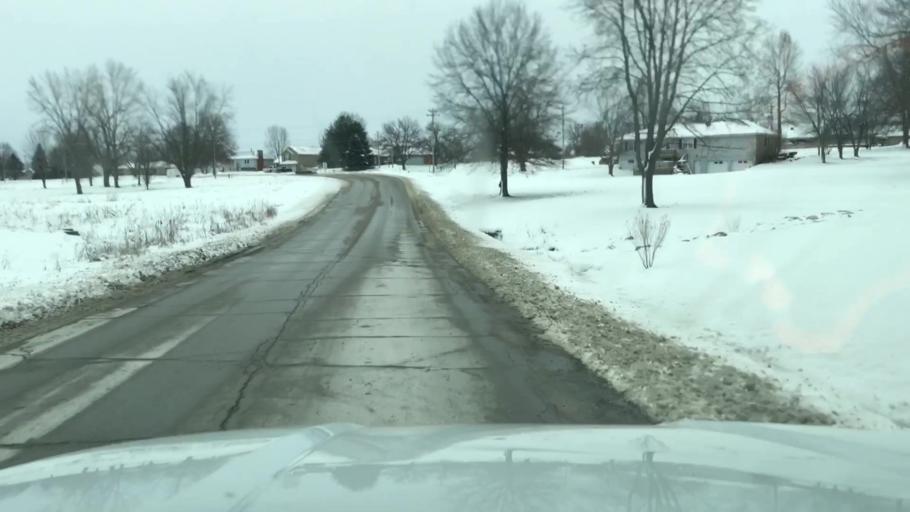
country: US
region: Missouri
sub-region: Clinton County
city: Cameron
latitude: 39.7436
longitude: -94.2270
